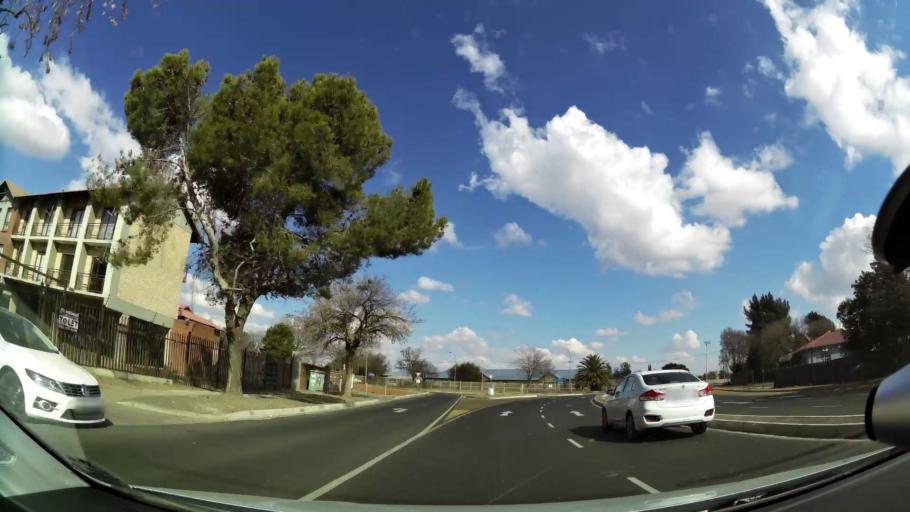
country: ZA
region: Orange Free State
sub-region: Mangaung Metropolitan Municipality
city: Bloemfontein
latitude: -29.1232
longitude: 26.1982
